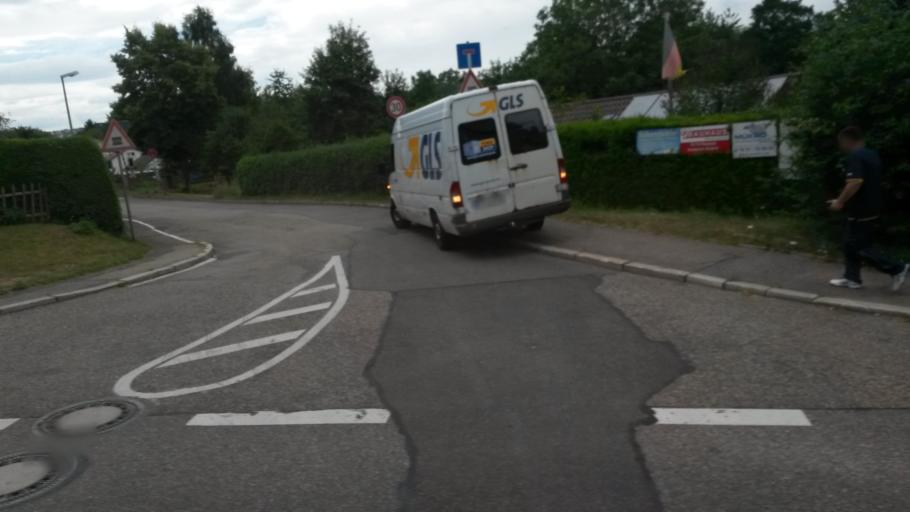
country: DE
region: Baden-Wuerttemberg
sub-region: Karlsruhe Region
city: Pforzheim
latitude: 48.8833
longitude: 8.6696
